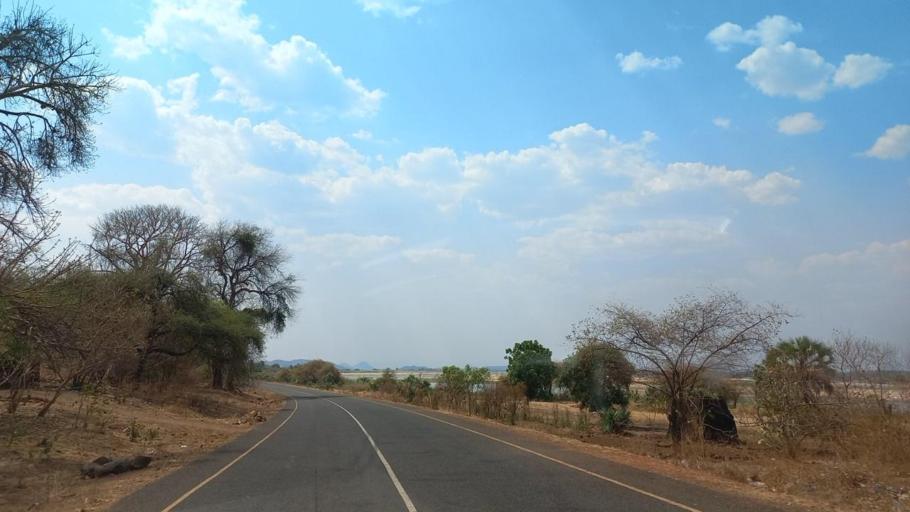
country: ZM
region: Lusaka
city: Luangwa
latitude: -15.3136
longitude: 30.3290
